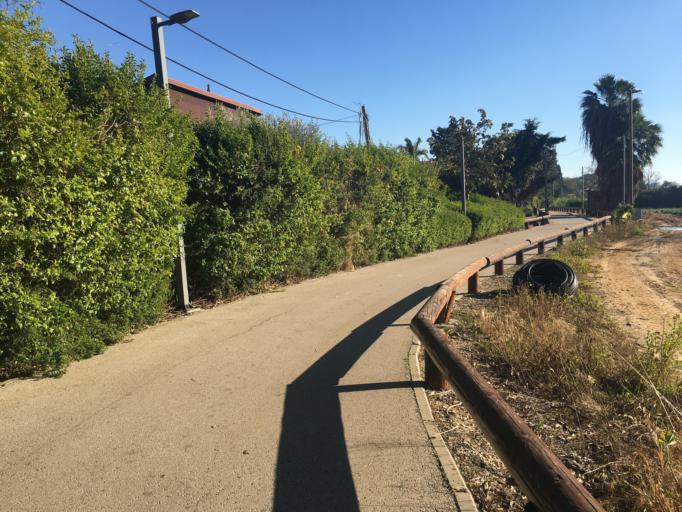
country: IL
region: Tel Aviv
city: Ramat HaSharon
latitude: 32.1444
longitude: 34.8265
